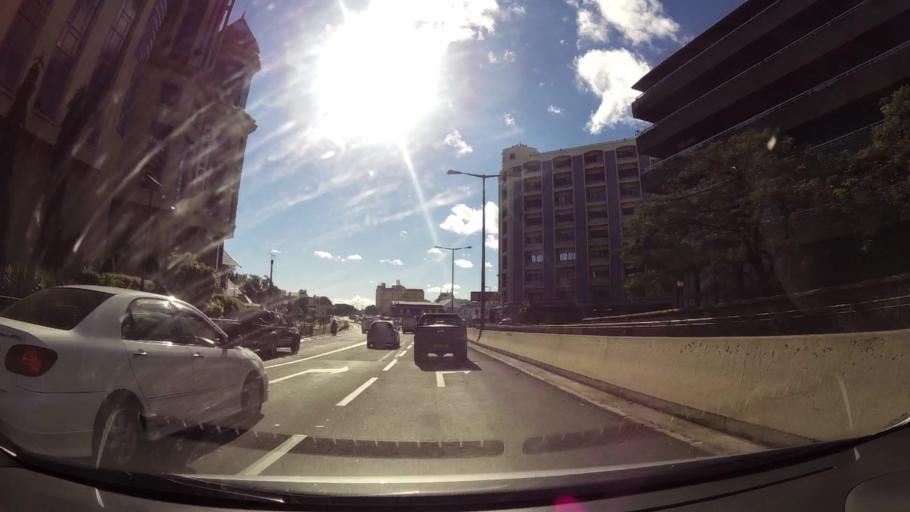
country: MU
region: Port Louis
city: Port Louis
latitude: -20.1619
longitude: 57.5002
